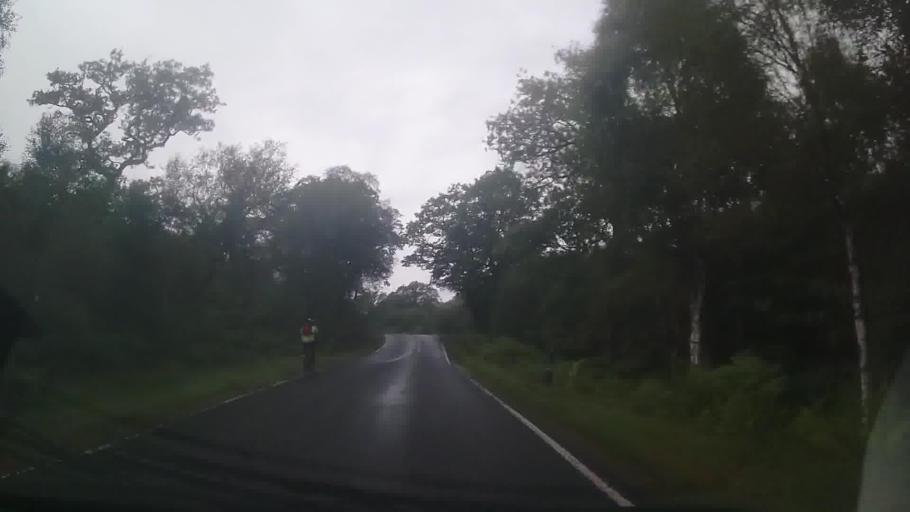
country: GB
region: Scotland
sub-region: Argyll and Bute
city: Isle Of Mull
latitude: 56.6972
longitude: -5.6861
